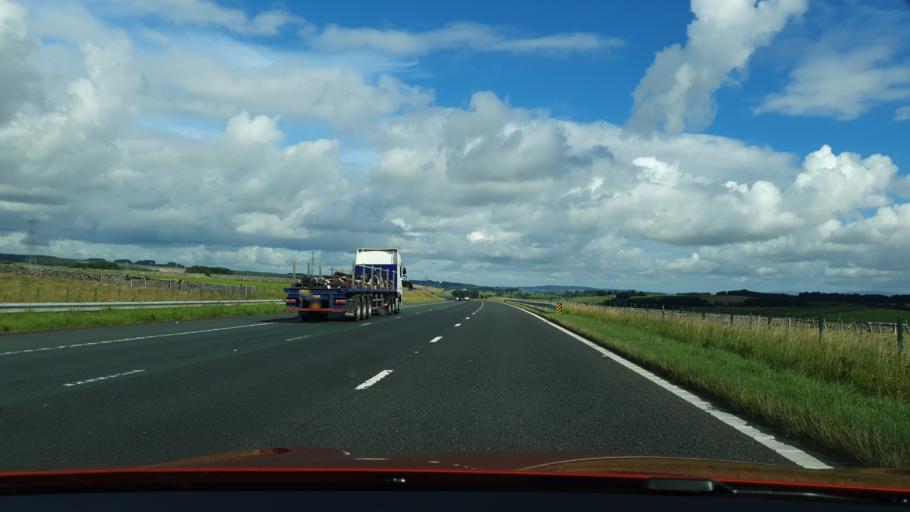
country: GB
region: England
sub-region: Cumbria
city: Penrith
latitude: 54.5397
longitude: -2.6631
